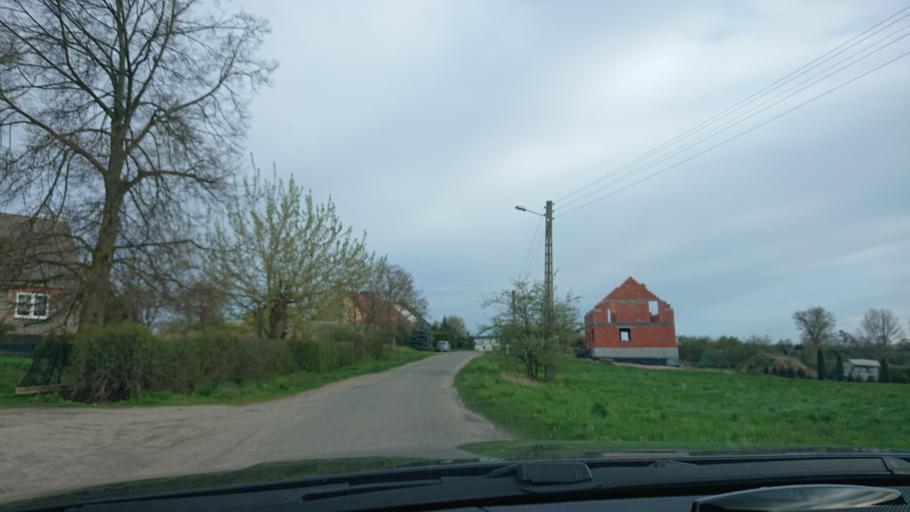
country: PL
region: Greater Poland Voivodeship
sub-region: Powiat gnieznienski
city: Lubowo
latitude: 52.5740
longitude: 17.4728
